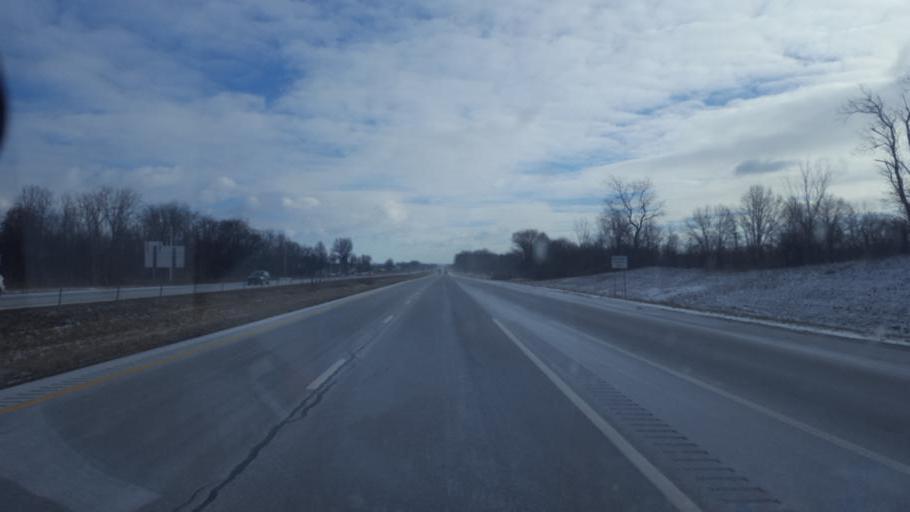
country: US
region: Ohio
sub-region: Fairfield County
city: Millersport
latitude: 39.9447
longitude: -82.5957
